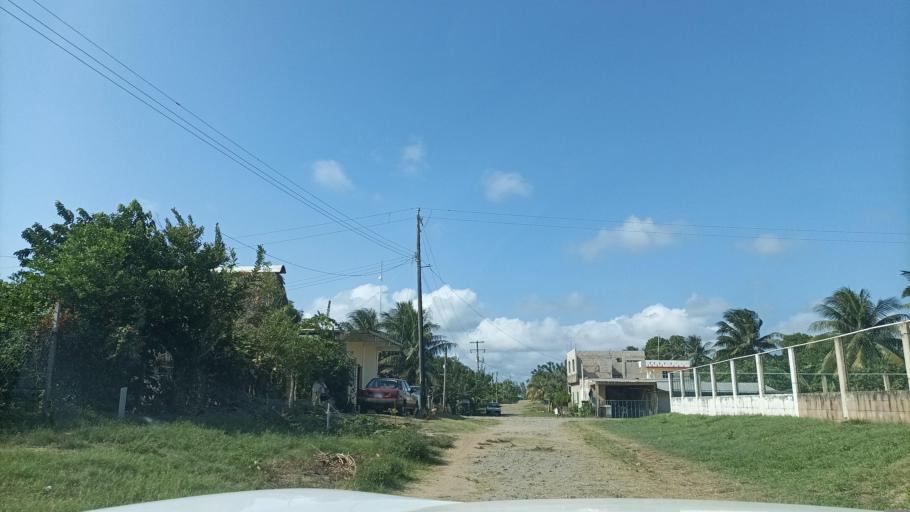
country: MX
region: Veracruz
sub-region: Coatzacoalcos
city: Fraccionamiento Ciudad Olmeca
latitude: 18.2135
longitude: -94.6117
